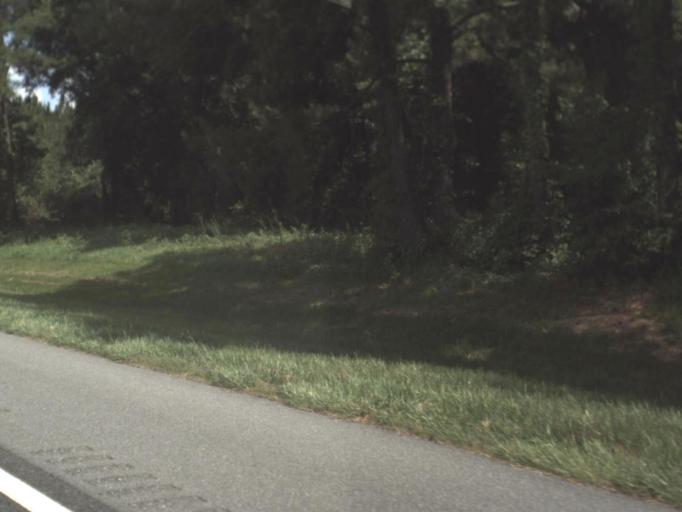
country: US
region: Florida
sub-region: Suwannee County
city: Wellborn
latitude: 30.2889
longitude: -82.7741
